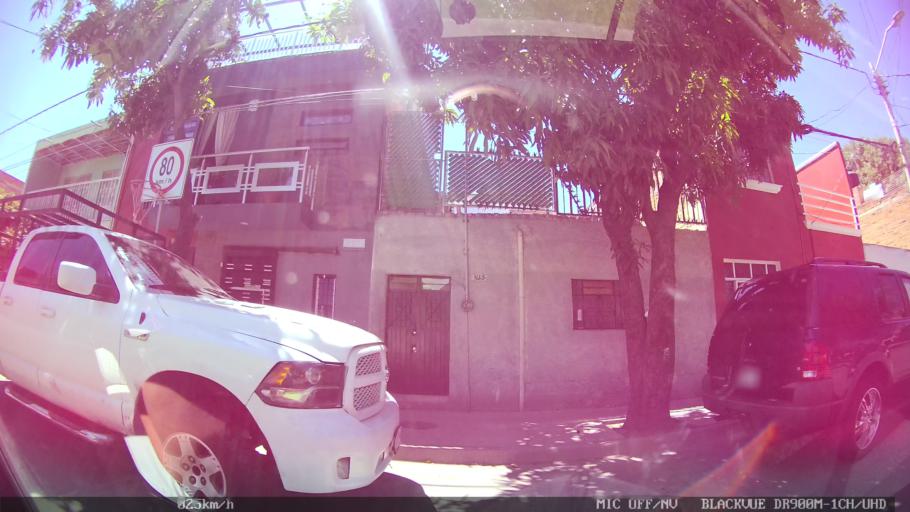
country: MX
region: Jalisco
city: Tlaquepaque
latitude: 20.6750
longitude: -103.2748
